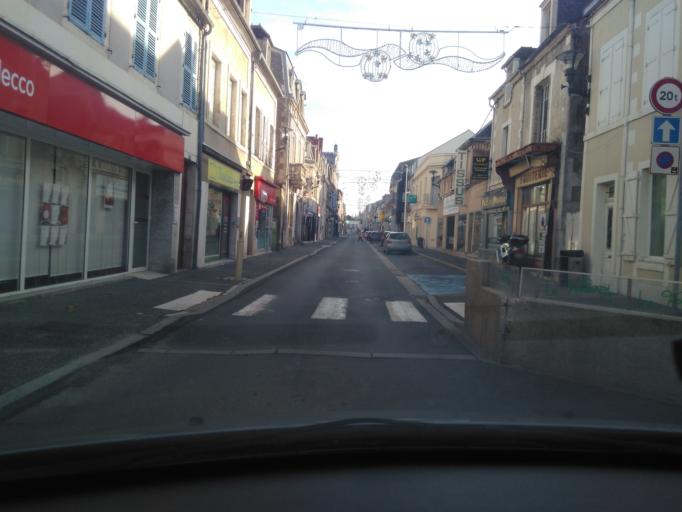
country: FR
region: Centre
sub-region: Departement du Cher
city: Saint-Amand-Montrond
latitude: 46.7236
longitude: 2.5004
